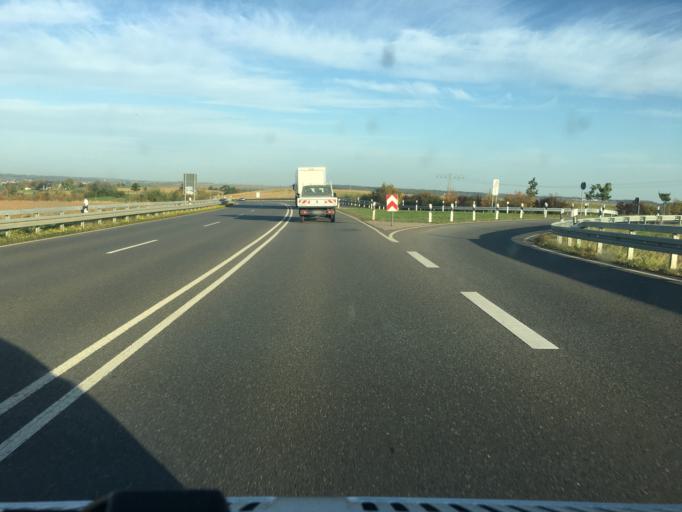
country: DE
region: Saxony
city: Lichtentanne
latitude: 50.6821
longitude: 12.4468
